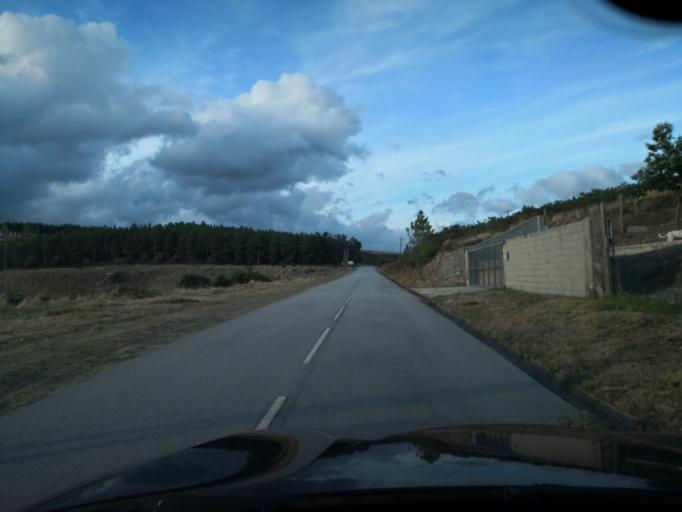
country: PT
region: Vila Real
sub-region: Santa Marta de Penaguiao
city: Santa Marta de Penaguiao
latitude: 41.2295
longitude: -7.8363
